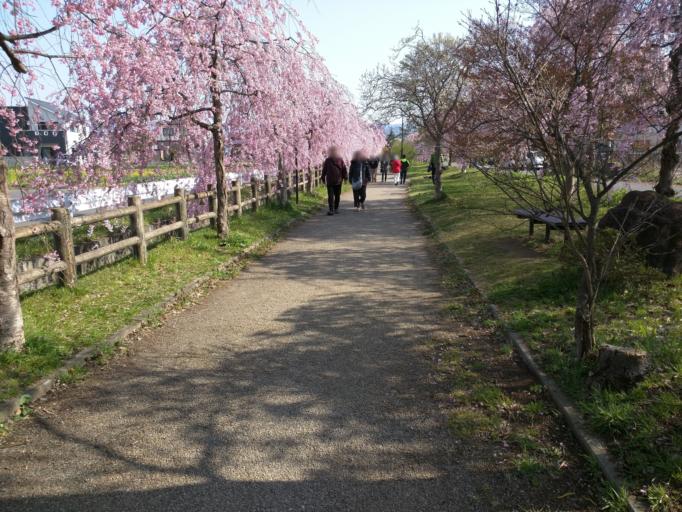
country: JP
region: Fukushima
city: Kitakata
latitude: 37.6581
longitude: 139.8678
